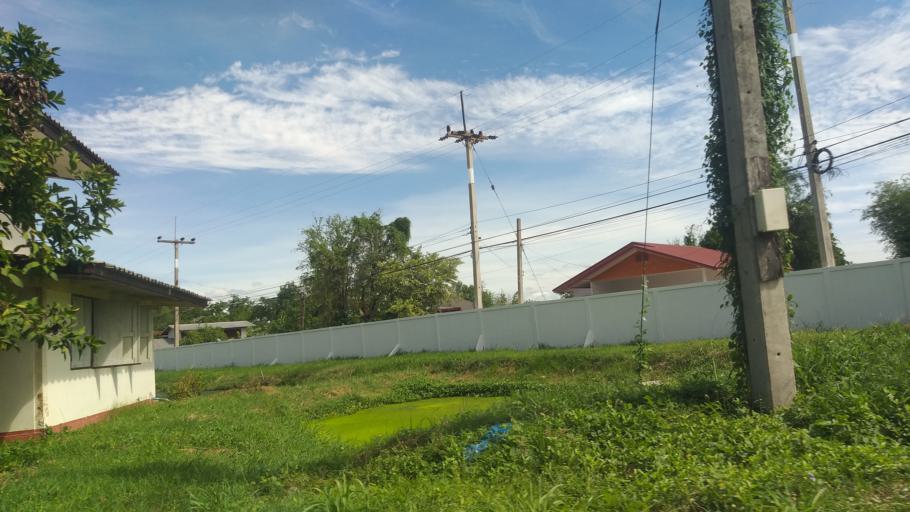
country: TH
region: Chaiyaphum
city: Ban Thaen
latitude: 16.4072
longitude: 102.3434
